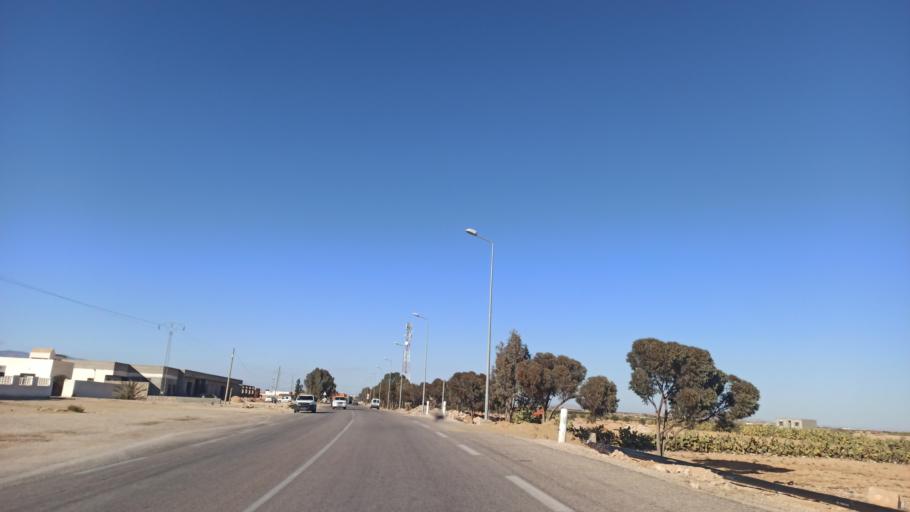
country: TN
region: Sidi Bu Zayd
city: Jilma
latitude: 35.2891
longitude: 9.4186
